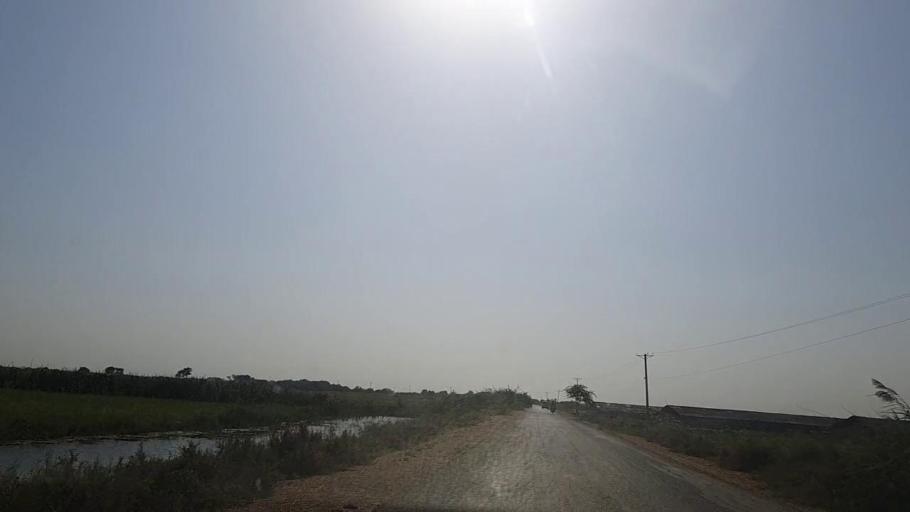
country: PK
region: Sindh
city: Jati
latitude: 24.4597
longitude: 68.2681
